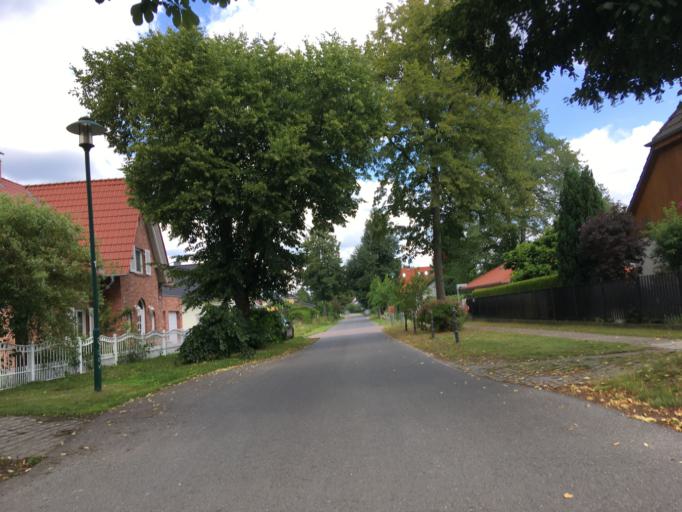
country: DE
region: Berlin
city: Buch
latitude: 52.6725
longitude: 13.5248
